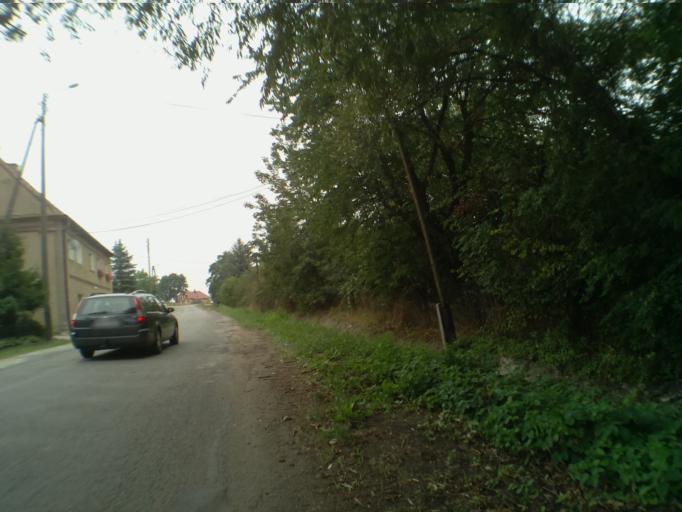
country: PL
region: Lower Silesian Voivodeship
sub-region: Powiat swidnicki
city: Swiebodzice
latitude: 50.9004
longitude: 16.3205
